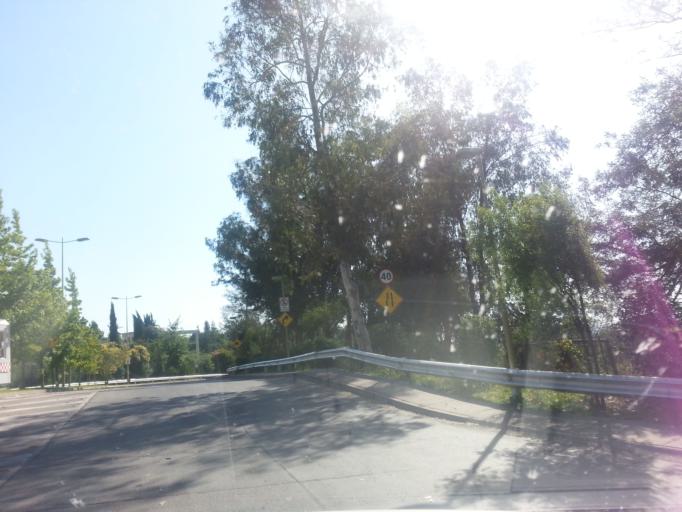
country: CL
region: Santiago Metropolitan
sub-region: Provincia de Santiago
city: Villa Presidente Frei, Nunoa, Santiago, Chile
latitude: -33.3781
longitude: -70.5011
